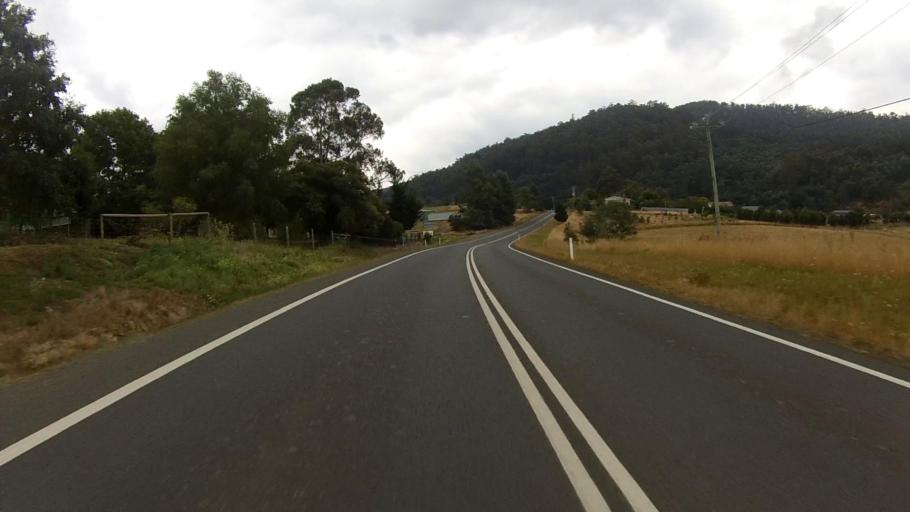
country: AU
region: Tasmania
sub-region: Huon Valley
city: Cygnet
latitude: -43.1441
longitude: 147.0644
